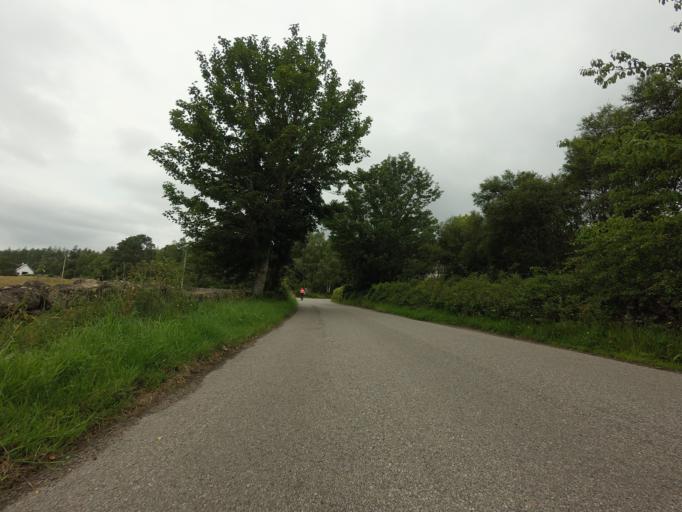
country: GB
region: Scotland
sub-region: Highland
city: Evanton
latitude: 57.8870
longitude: -4.3885
